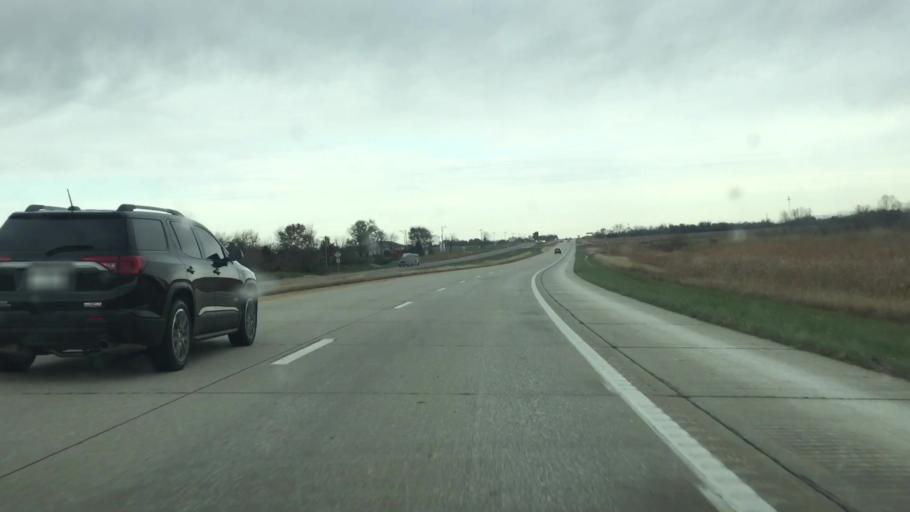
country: US
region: Missouri
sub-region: Saint Clair County
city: Osceola
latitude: 38.1476
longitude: -93.7227
